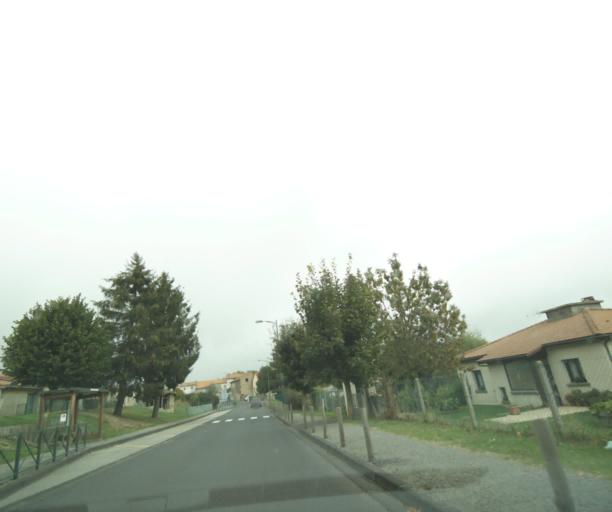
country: FR
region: Auvergne
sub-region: Departement du Puy-de-Dome
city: Saint-Genes-Champanelle
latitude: 45.7190
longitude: 3.0192
